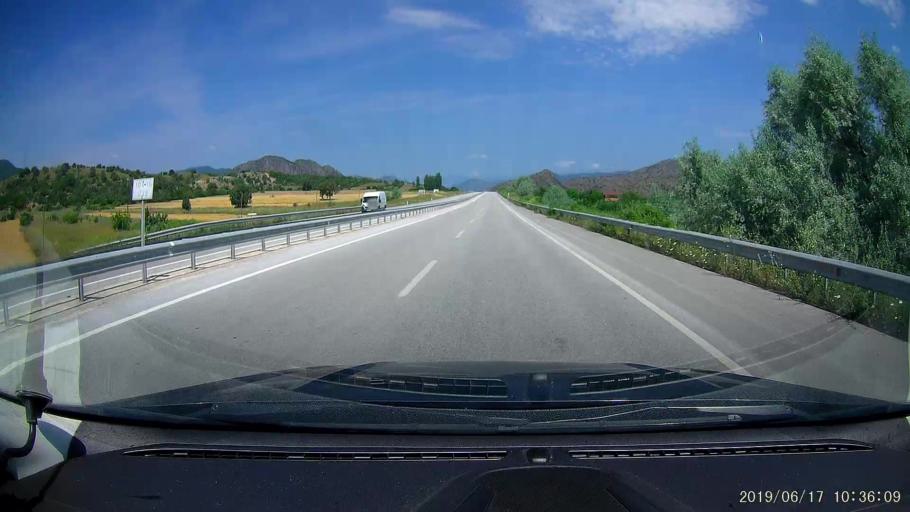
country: TR
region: Corum
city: Osmancik
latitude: 40.9750
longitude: 34.6869
